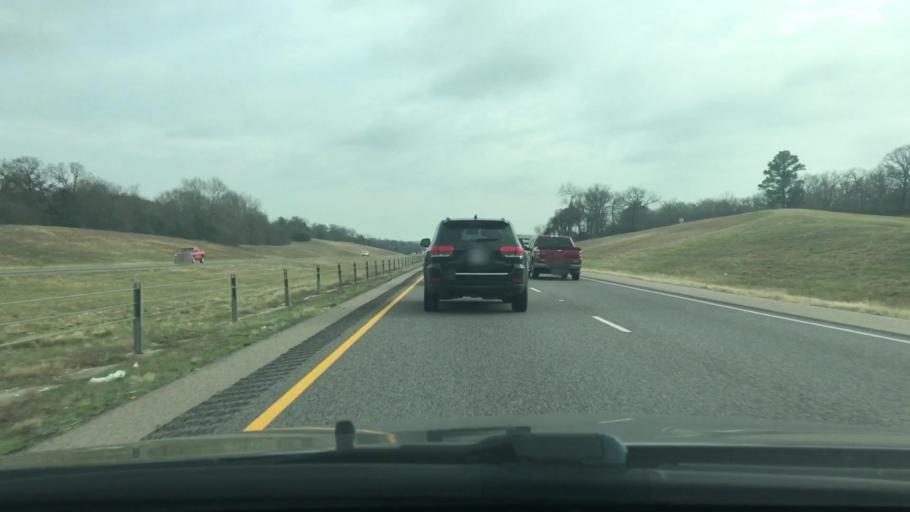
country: US
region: Texas
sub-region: Leon County
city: Buffalo
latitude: 31.5189
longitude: -96.1089
